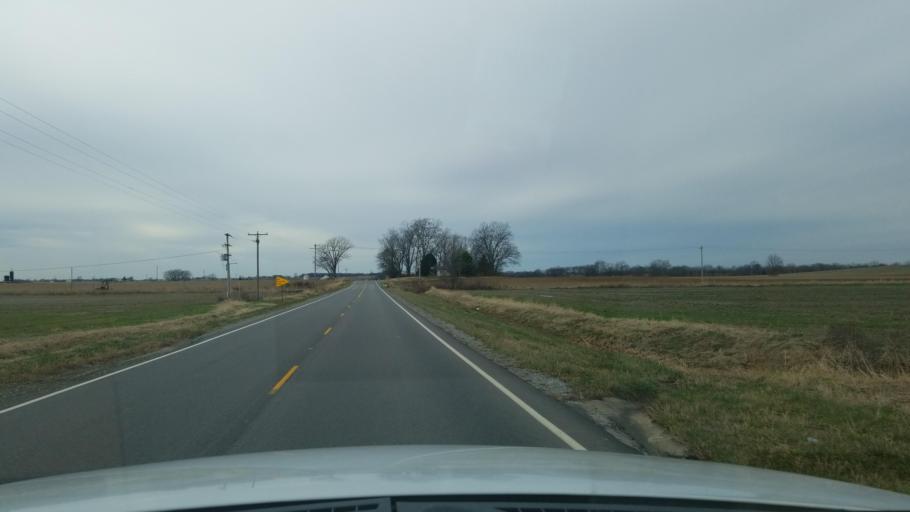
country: US
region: Illinois
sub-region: White County
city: Norris City
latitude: 37.9076
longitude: -88.1614
